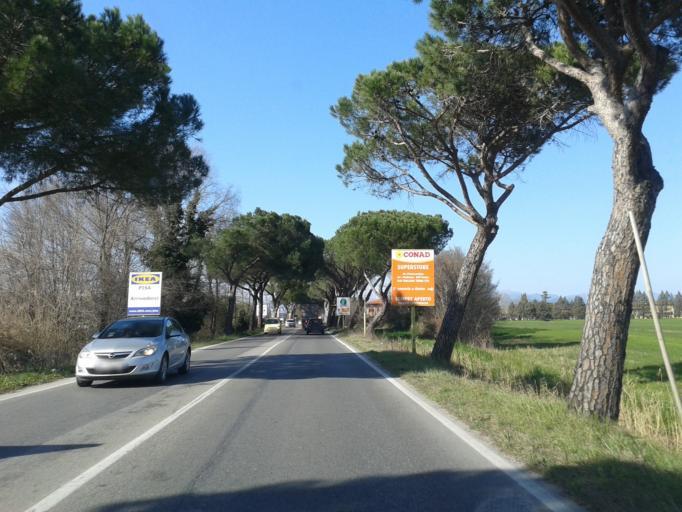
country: IT
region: Tuscany
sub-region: Province of Pisa
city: Madonna dell'Acqua
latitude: 43.7205
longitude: 10.3807
